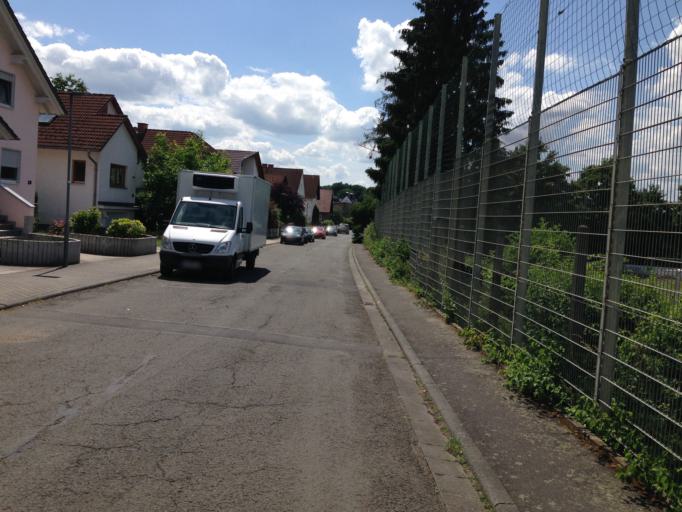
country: DE
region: Hesse
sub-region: Regierungsbezirk Giessen
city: Heuchelheim
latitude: 50.5619
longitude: 8.6467
